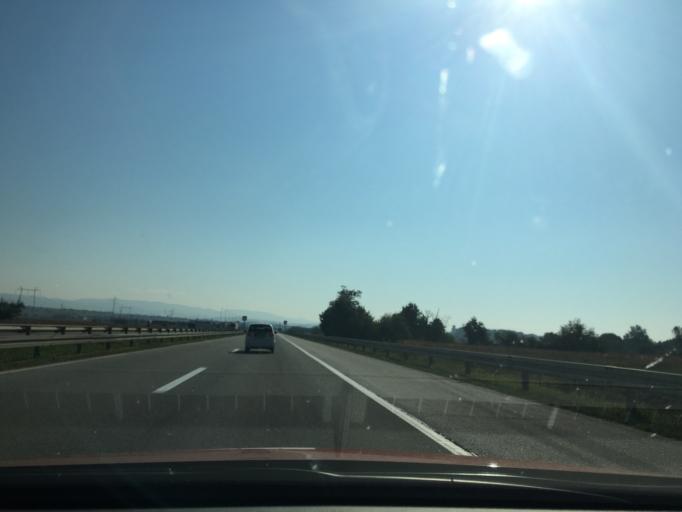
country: RS
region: Central Serbia
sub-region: Pomoravski Okrug
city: Cuprija
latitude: 43.9560
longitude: 21.3564
